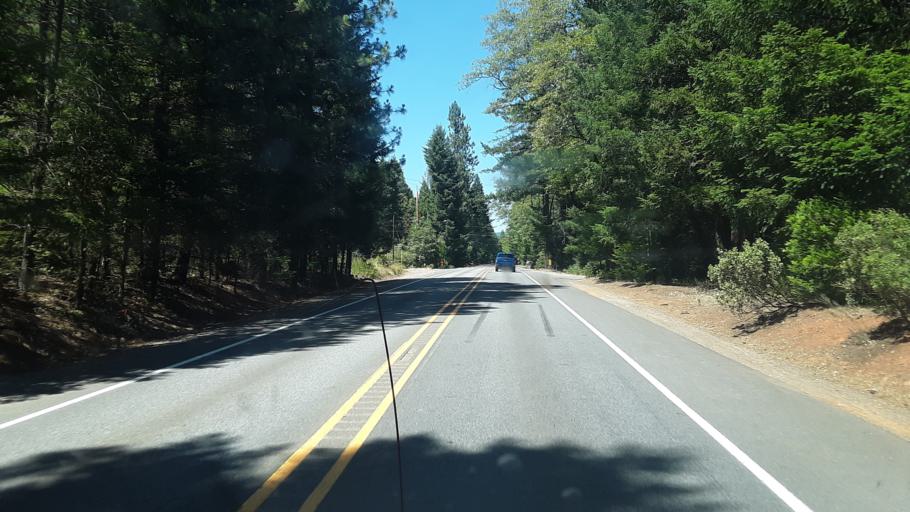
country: US
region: Oregon
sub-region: Josephine County
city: Cave Junction
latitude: 42.3000
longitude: -123.6118
